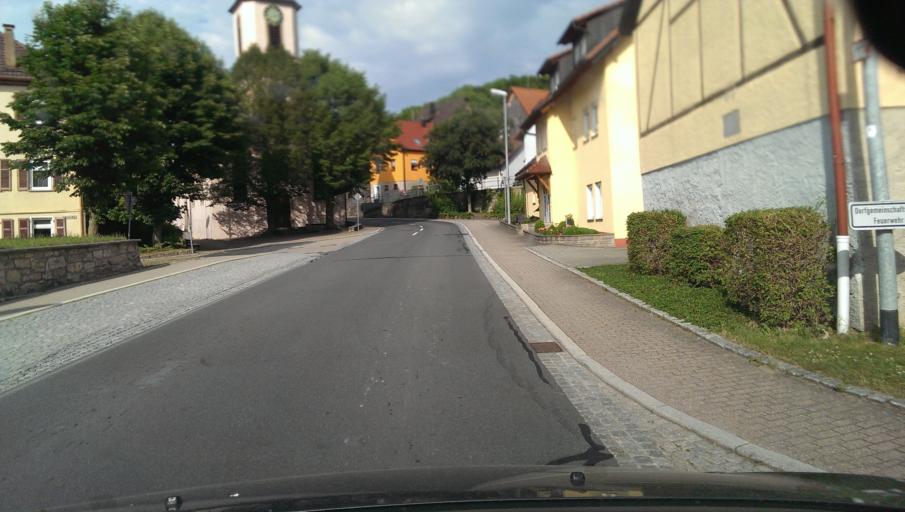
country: DE
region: Baden-Wuerttemberg
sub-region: Regierungsbezirk Stuttgart
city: Dorzbach
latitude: 49.4029
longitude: 9.7226
